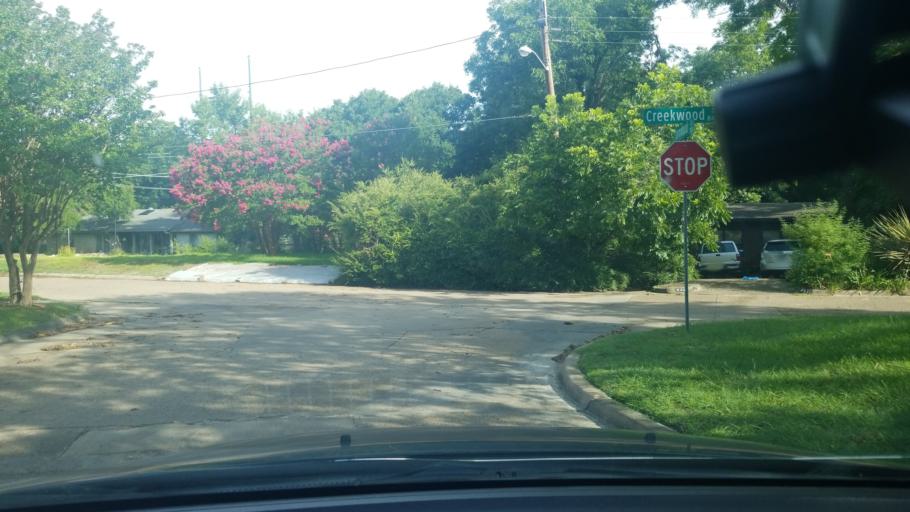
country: US
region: Texas
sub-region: Dallas County
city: Highland Park
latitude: 32.8109
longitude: -96.7074
